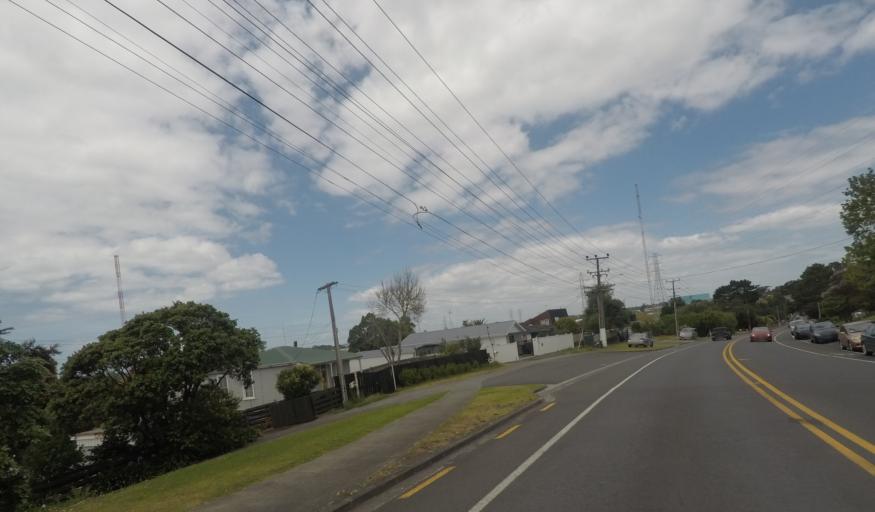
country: NZ
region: Auckland
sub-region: Auckland
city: Rosebank
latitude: -36.8450
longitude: 174.6258
